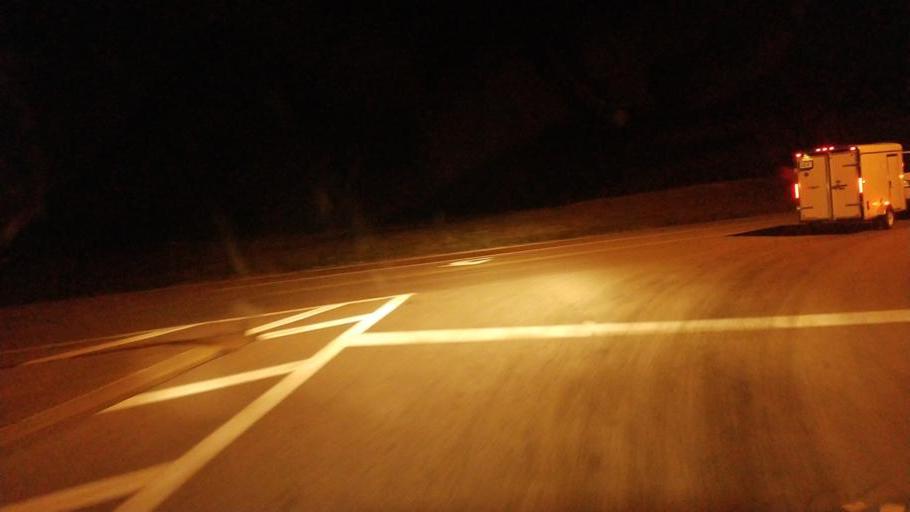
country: US
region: Illinois
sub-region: Henderson County
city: Oquawka
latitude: 40.7706
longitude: -90.9041
